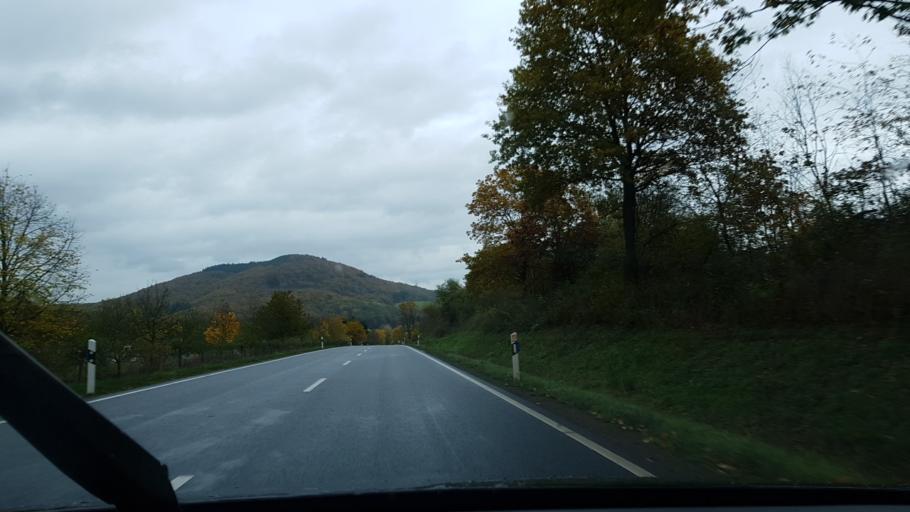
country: DE
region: Rheinland-Pfalz
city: Sehlem
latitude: 49.9169
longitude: 6.8302
